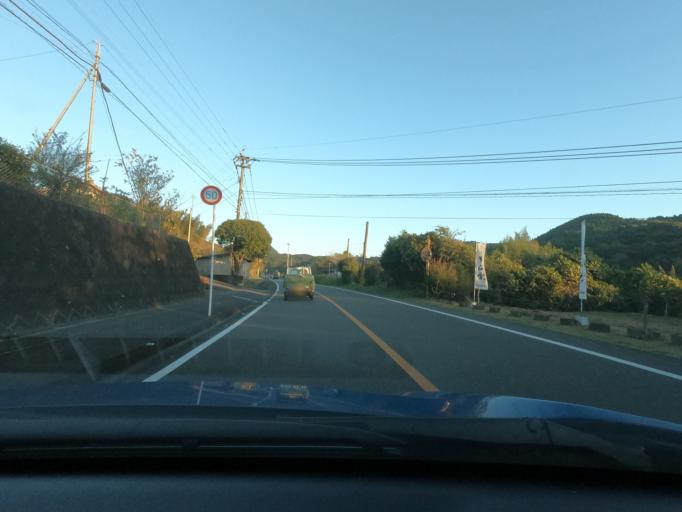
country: JP
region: Kagoshima
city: Satsumasendai
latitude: 31.7916
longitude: 130.4584
